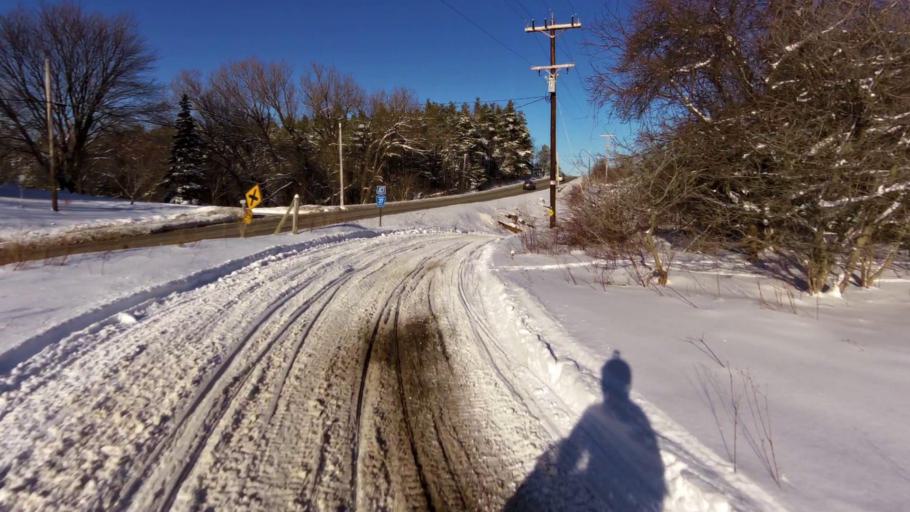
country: US
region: New York
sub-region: Chautauqua County
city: Mayville
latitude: 42.2794
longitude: -79.4448
